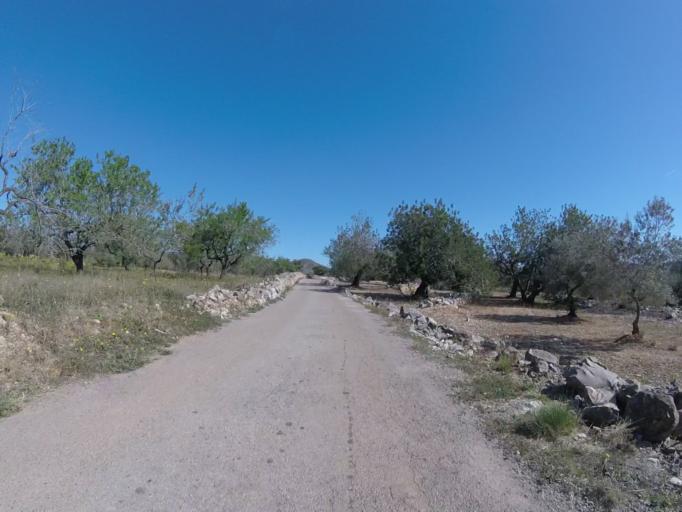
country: ES
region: Valencia
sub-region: Provincia de Castello
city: Santa Magdalena de Pulpis
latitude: 40.3569
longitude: 0.2851
